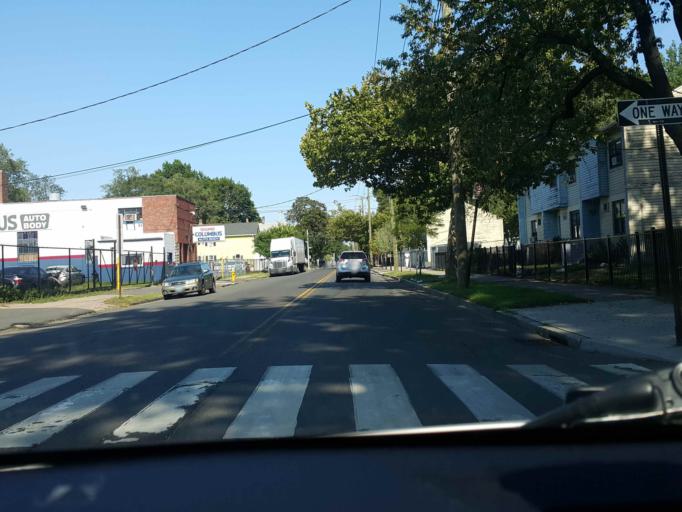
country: US
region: Connecticut
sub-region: New Haven County
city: New Haven
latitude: 41.2976
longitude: -72.9430
